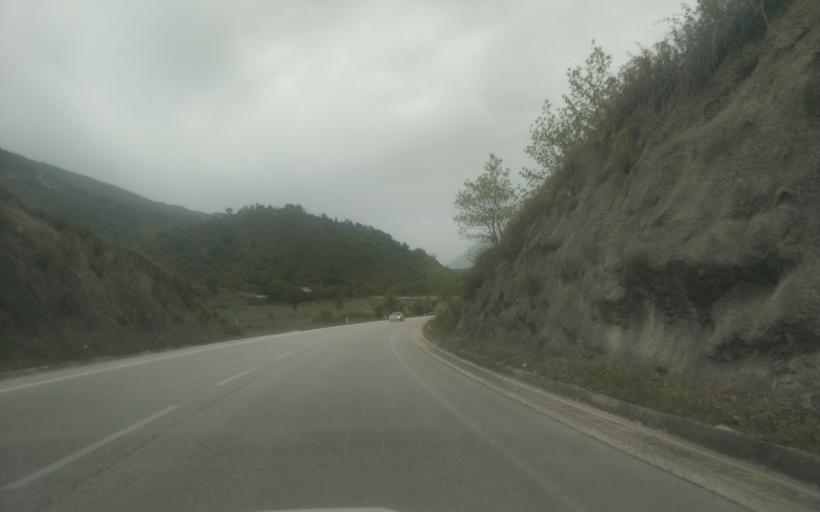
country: AL
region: Gjirokaster
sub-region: Rrethi i Gjirokastres
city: Picar
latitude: 40.2057
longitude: 20.0893
